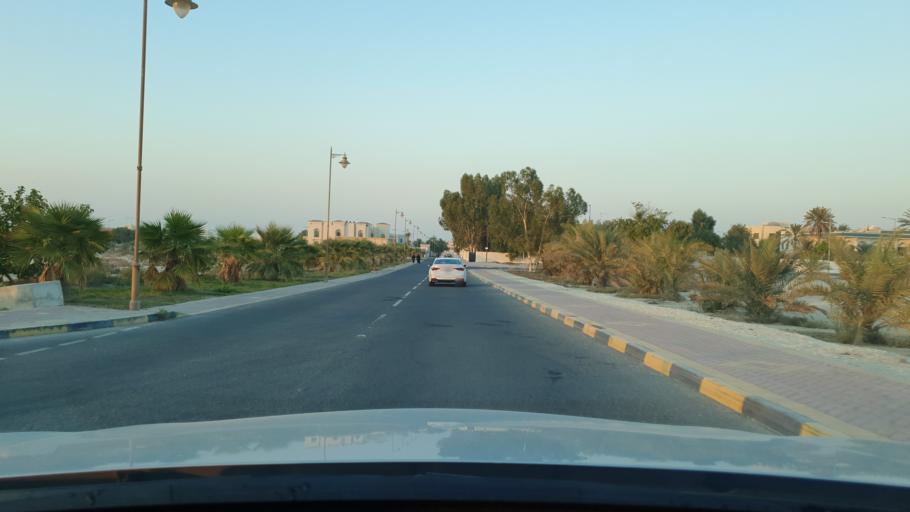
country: BH
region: Northern
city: Ar Rifa'
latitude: 26.1360
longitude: 50.5323
